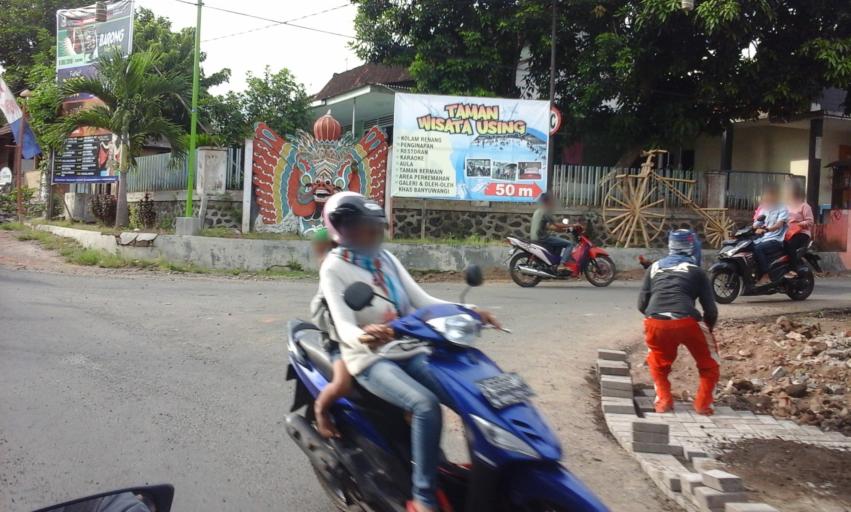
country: ID
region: East Java
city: Krajan
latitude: -8.2050
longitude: 114.3199
